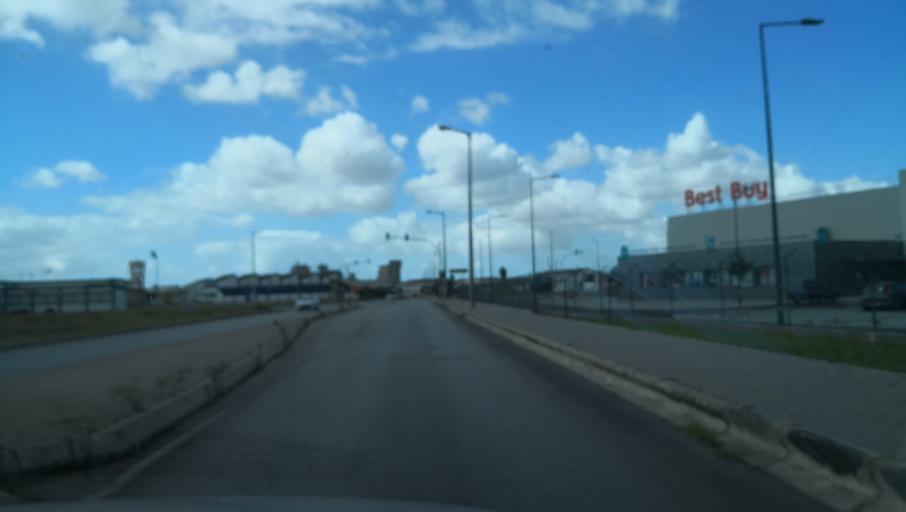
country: PT
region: Setubal
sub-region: Barreiro
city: Barreiro
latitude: 38.6670
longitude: -9.0604
